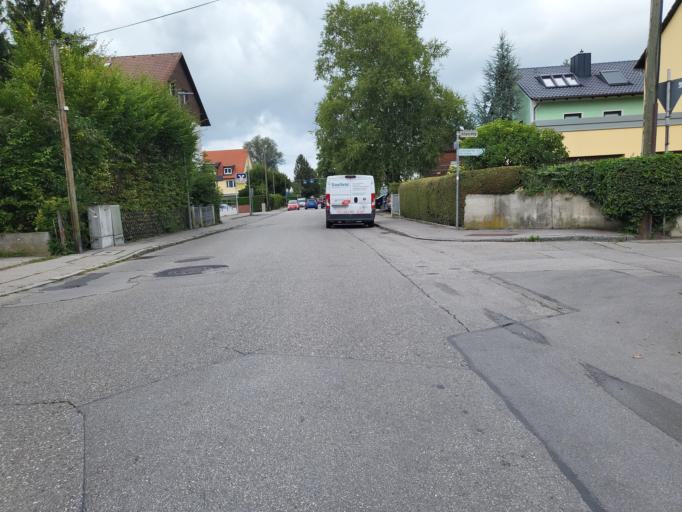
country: DE
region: Bavaria
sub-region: Upper Bavaria
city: Olching
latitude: 48.2145
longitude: 11.3215
